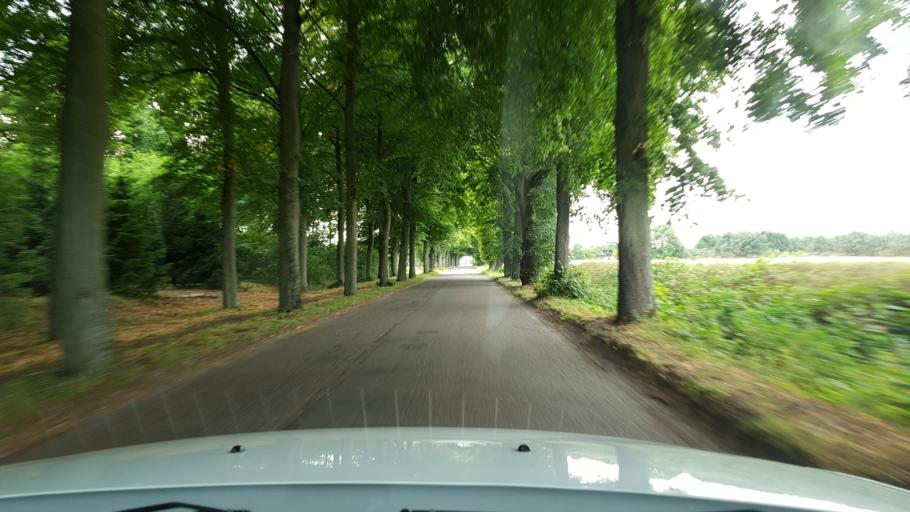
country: PL
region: West Pomeranian Voivodeship
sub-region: Powiat drawski
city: Wierzchowo
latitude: 53.4563
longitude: 16.1103
